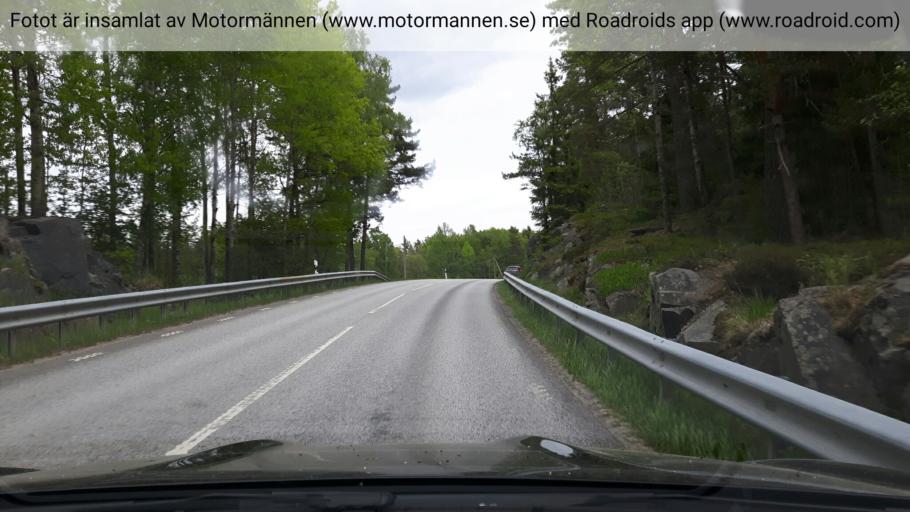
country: SE
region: Stockholm
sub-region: Vaxholms Kommun
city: Resaro
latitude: 59.5481
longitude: 18.4873
